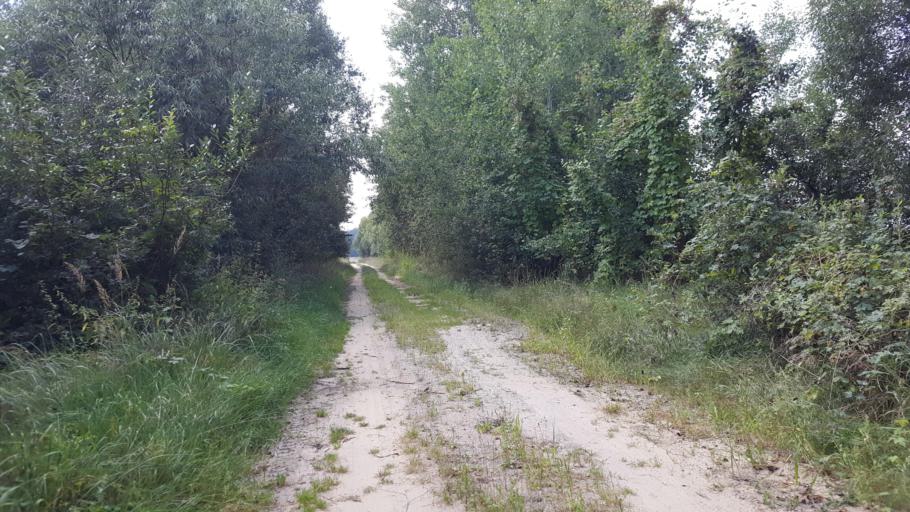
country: PL
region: Podlasie
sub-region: Powiat hajnowski
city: Hajnowka
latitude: 52.5753
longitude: 23.5667
